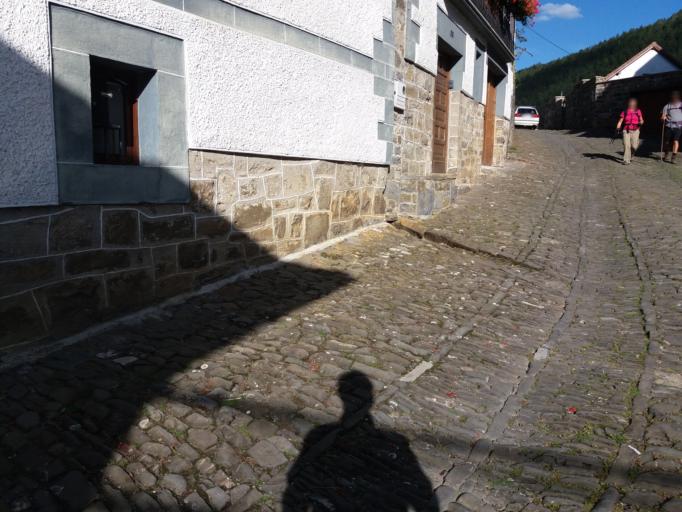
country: ES
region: Navarre
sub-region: Provincia de Navarra
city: Oronz
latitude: 42.9065
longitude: -1.0909
